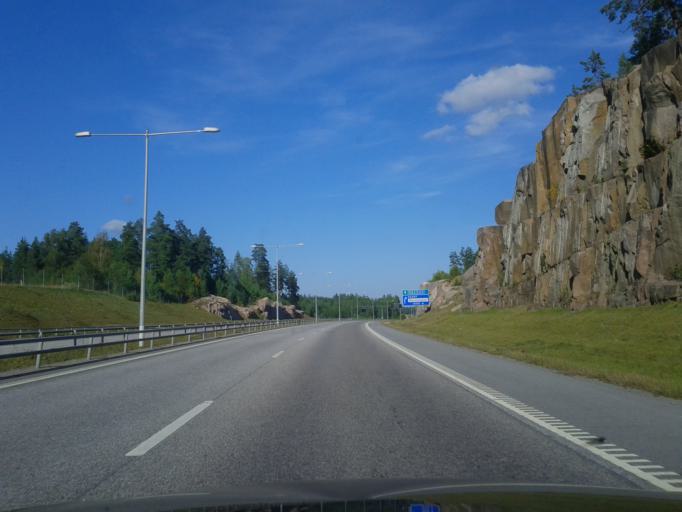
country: SE
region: Stockholm
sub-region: Sollentuna Kommun
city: Sollentuna
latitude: 59.4638
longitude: 17.9710
